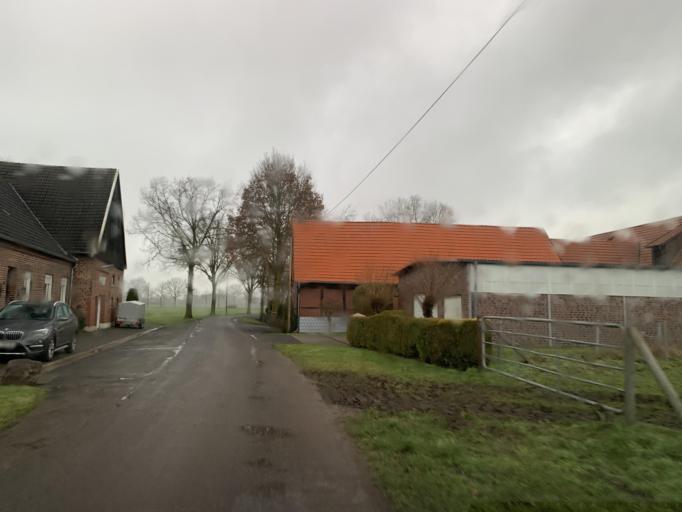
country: DE
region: North Rhine-Westphalia
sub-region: Regierungsbezirk Munster
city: Senden
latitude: 51.9018
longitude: 7.5328
